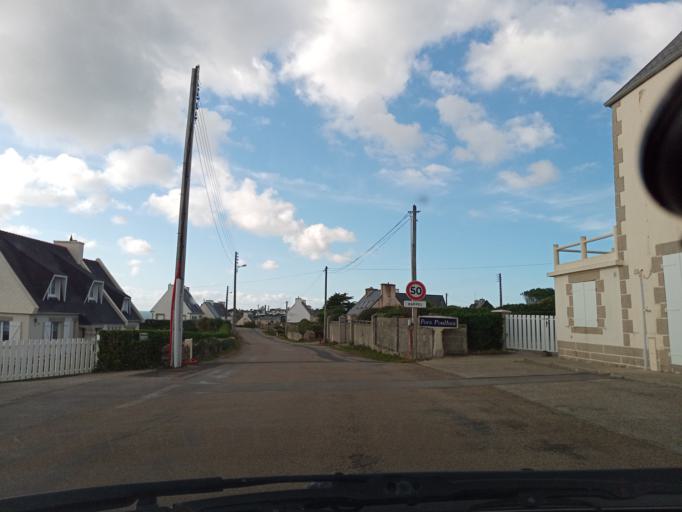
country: FR
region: Brittany
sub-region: Departement du Finistere
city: Plozevet
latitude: 47.9832
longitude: -4.4555
